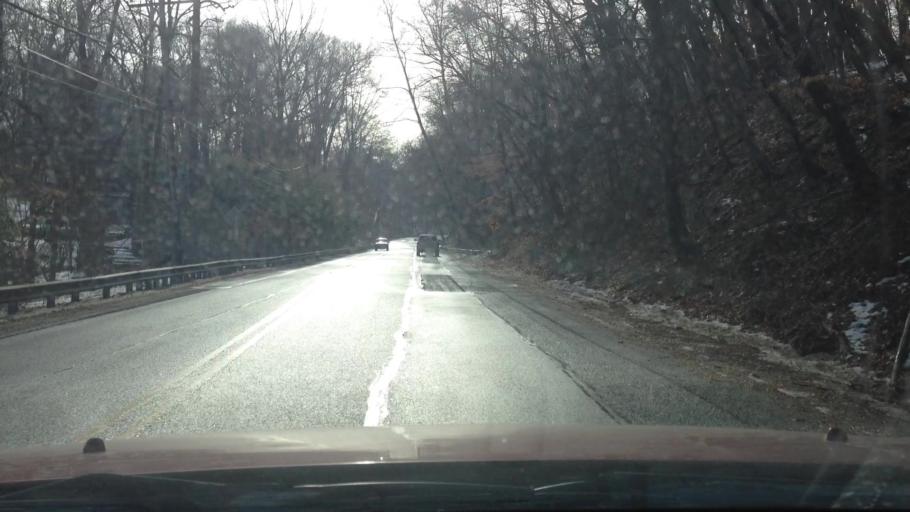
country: US
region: Pennsylvania
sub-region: Montgomery County
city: Narberth
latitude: 40.0393
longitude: -75.2529
